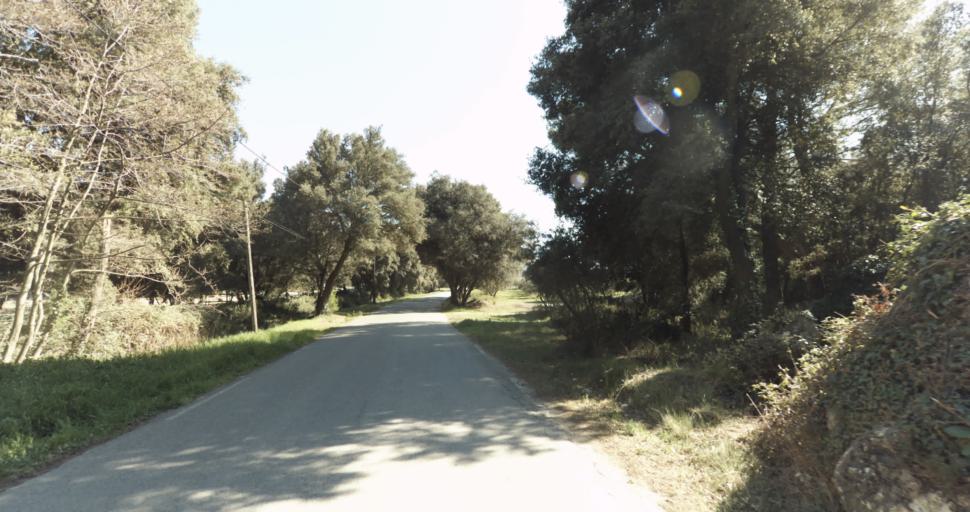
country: FR
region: Provence-Alpes-Cote d'Azur
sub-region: Departement des Bouches-du-Rhone
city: Pelissanne
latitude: 43.6491
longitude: 5.1808
